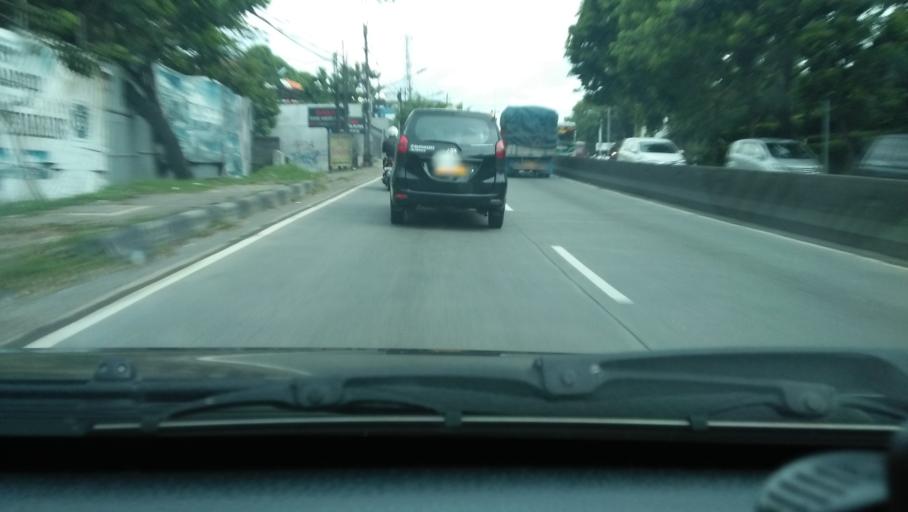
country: ID
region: Central Java
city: Ungaran
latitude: -7.0783
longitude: 110.4115
